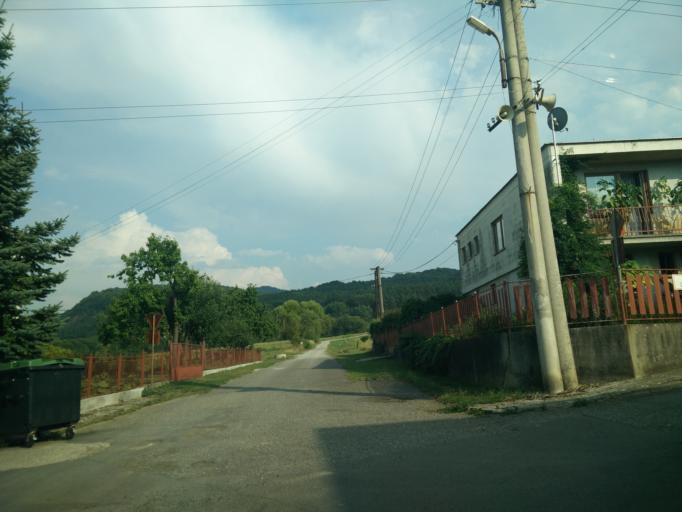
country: SK
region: Banskobystricky
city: Ziar nad Hronom
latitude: 48.5344
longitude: 18.7899
